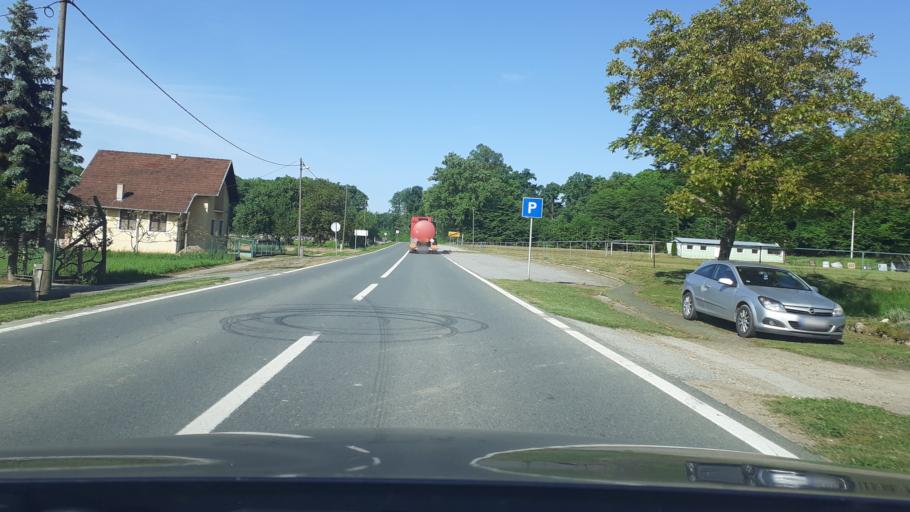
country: HR
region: Brodsko-Posavska
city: Batrina
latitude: 45.2104
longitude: 17.6877
